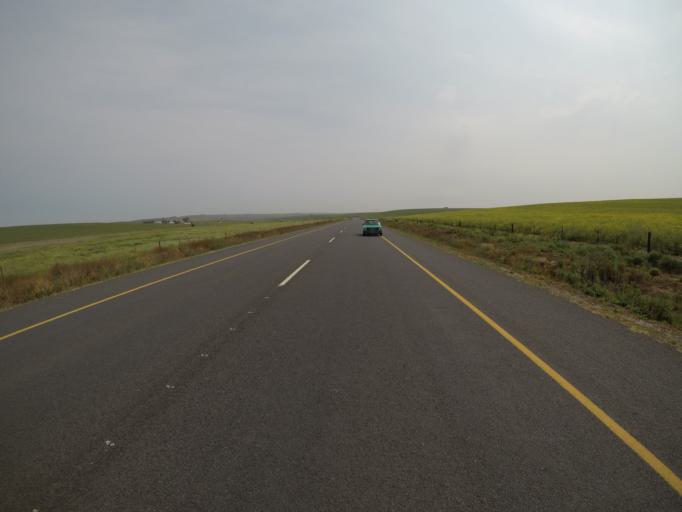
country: ZA
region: Western Cape
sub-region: West Coast District Municipality
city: Malmesbury
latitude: -33.4608
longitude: 18.7860
